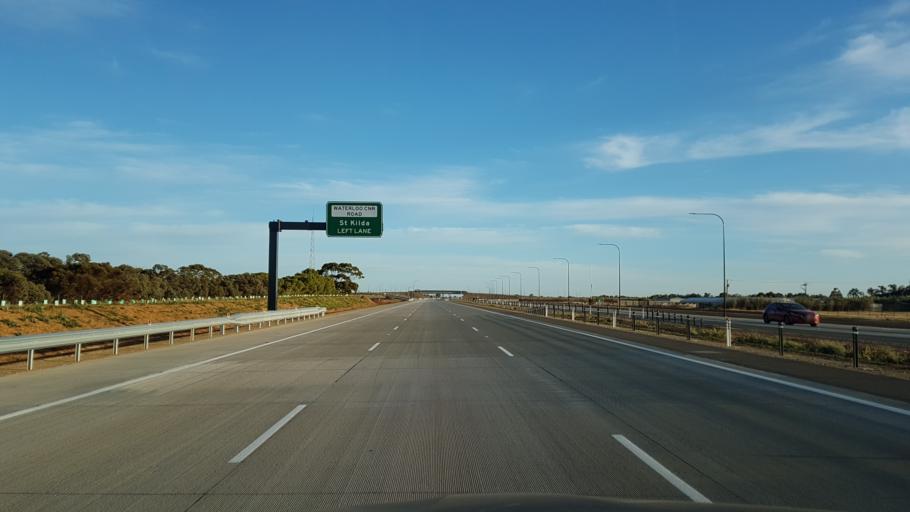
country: AU
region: South Australia
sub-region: Salisbury
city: Salisbury
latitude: -34.7412
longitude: 138.5794
